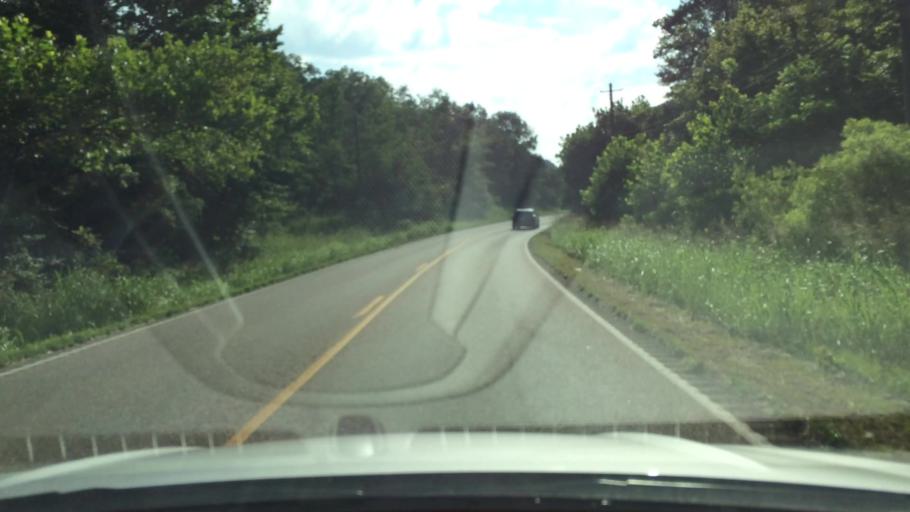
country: US
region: Tennessee
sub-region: Sevier County
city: Sevierville
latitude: 35.9218
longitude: -83.6137
